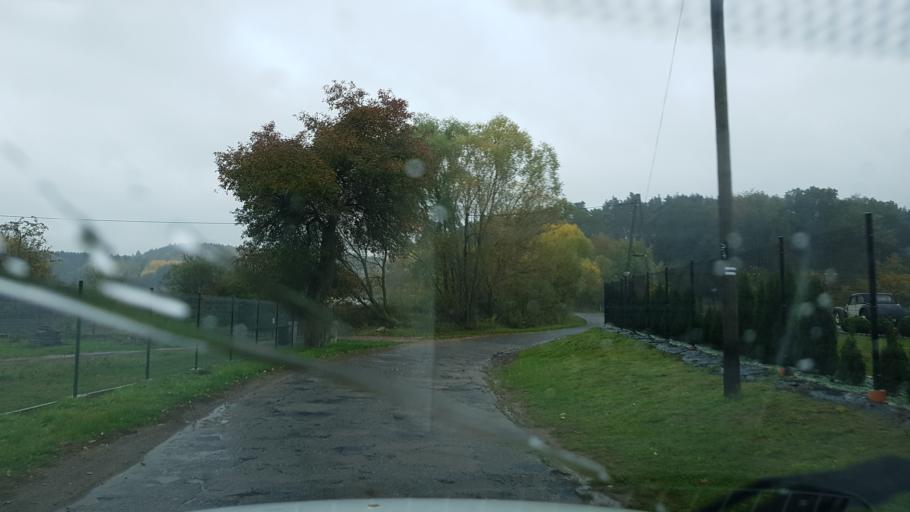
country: PL
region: West Pomeranian Voivodeship
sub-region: Powiat mysliborski
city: Barlinek
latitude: 53.0110
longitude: 15.2253
